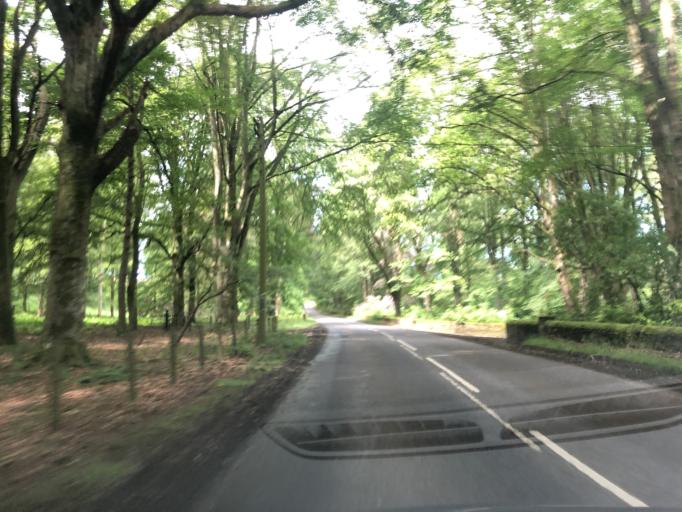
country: GB
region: Scotland
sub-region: Angus
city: Kirriemuir
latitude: 56.7130
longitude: -2.9834
